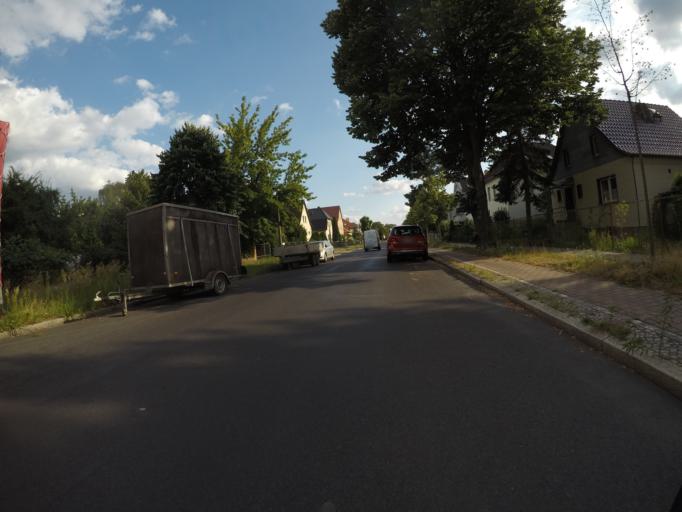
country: DE
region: Berlin
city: Kaulsdorf
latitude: 52.5169
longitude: 13.5938
